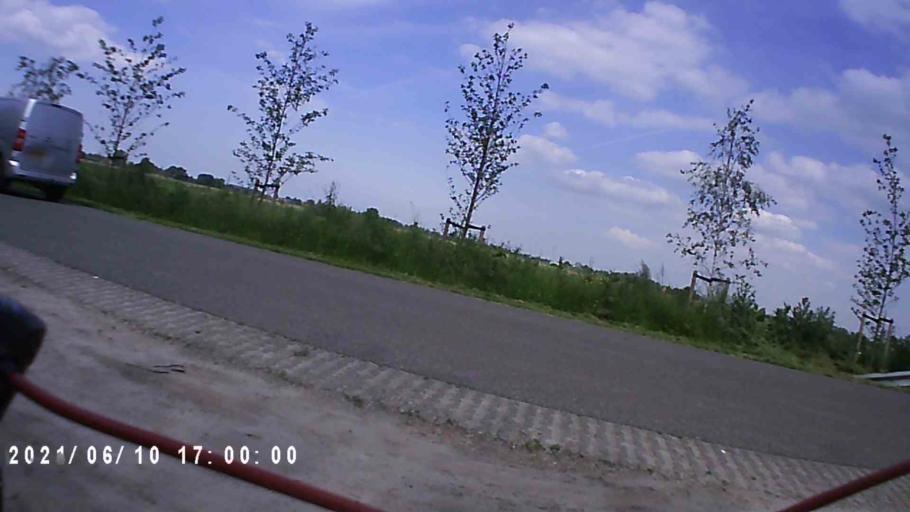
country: NL
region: Friesland
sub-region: Gemeente Kollumerland en Nieuwkruisland
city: Kollum
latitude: 53.2705
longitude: 6.1577
